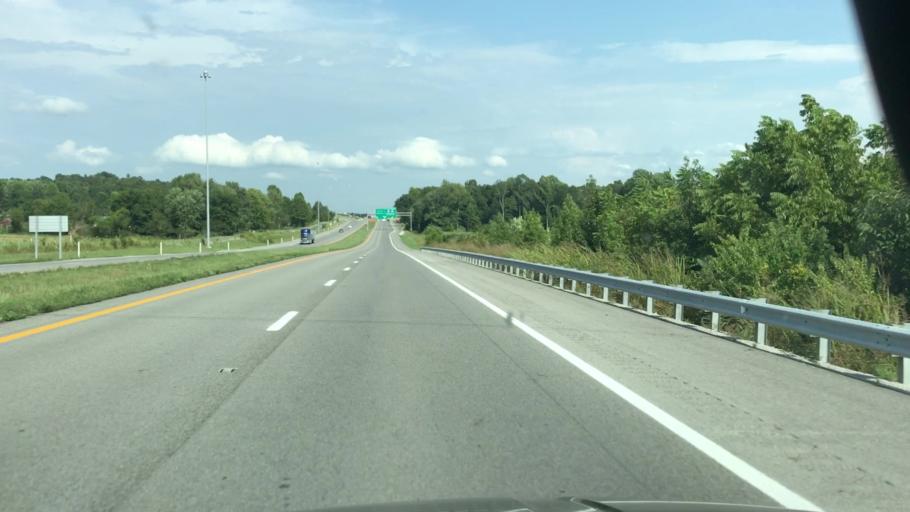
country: US
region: Kentucky
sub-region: Hopkins County
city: Nortonville
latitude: 37.2126
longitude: -87.4638
